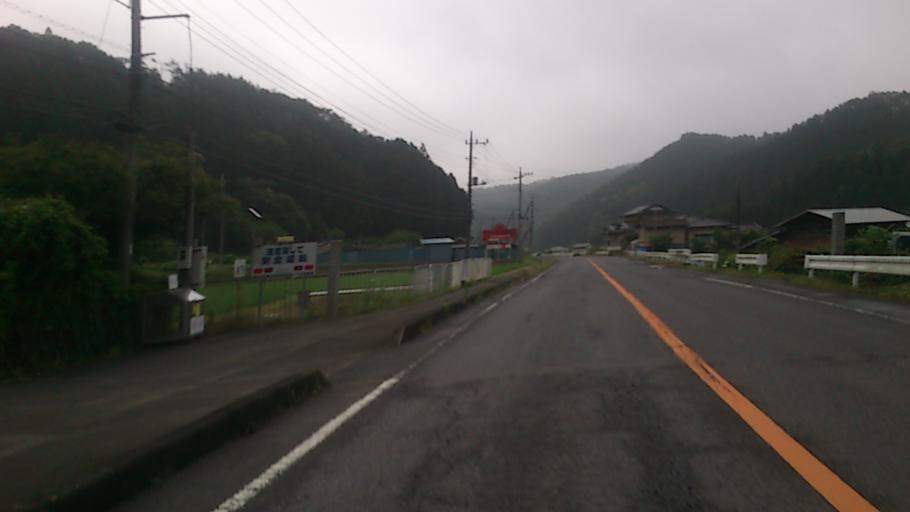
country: JP
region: Tochigi
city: Karasuyama
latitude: 36.6569
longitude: 140.2587
